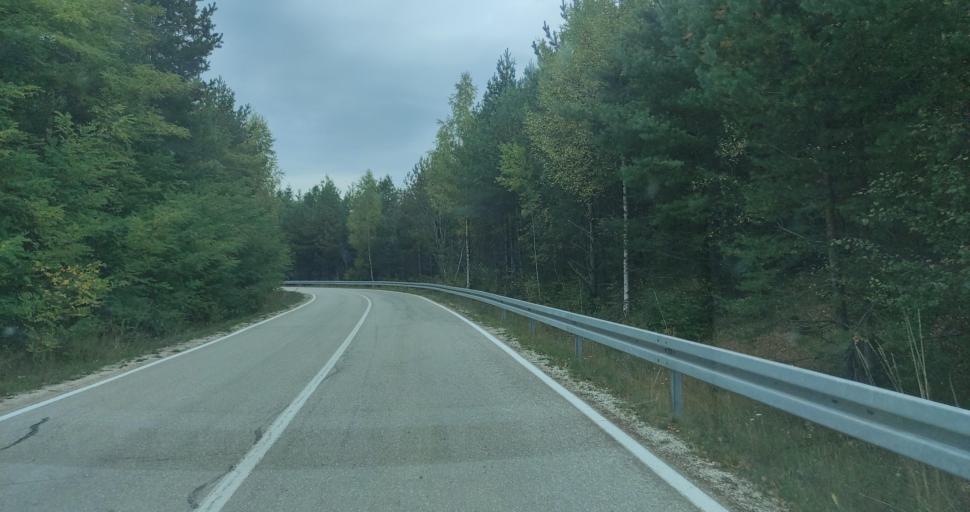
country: RS
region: Central Serbia
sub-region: Jablanicki Okrug
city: Crna Trava
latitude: 42.6955
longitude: 22.3253
